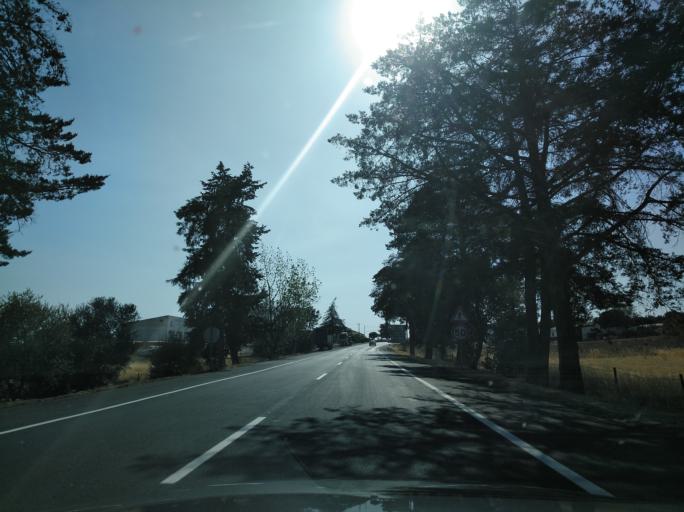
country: ES
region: Andalusia
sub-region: Provincia de Huelva
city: Rosal de la Frontera
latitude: 37.9503
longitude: -7.2974
